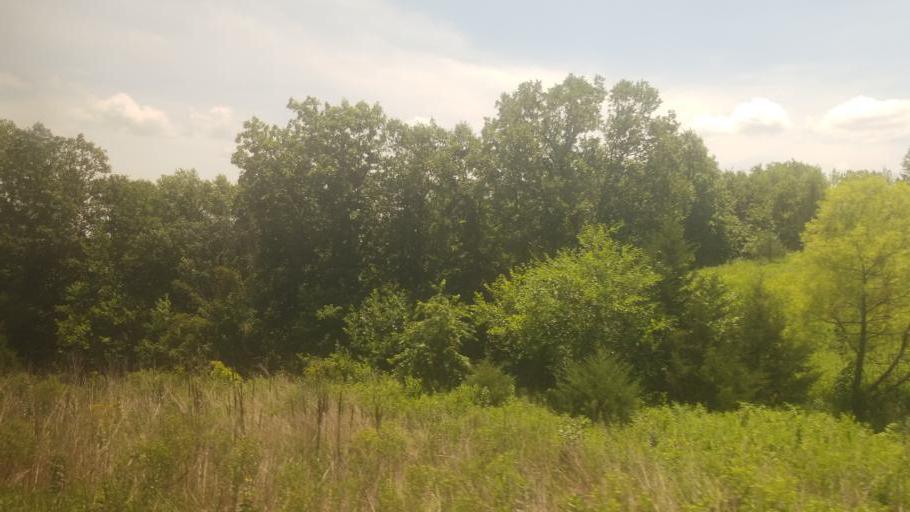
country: US
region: Missouri
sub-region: Linn County
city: Marceline
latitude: 39.8687
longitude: -92.7805
